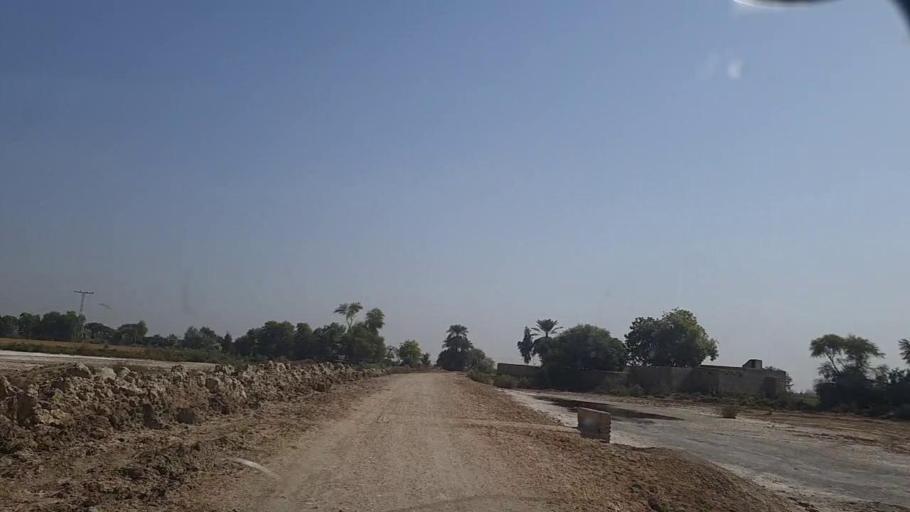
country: PK
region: Sindh
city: Thul
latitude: 28.1128
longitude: 68.7246
